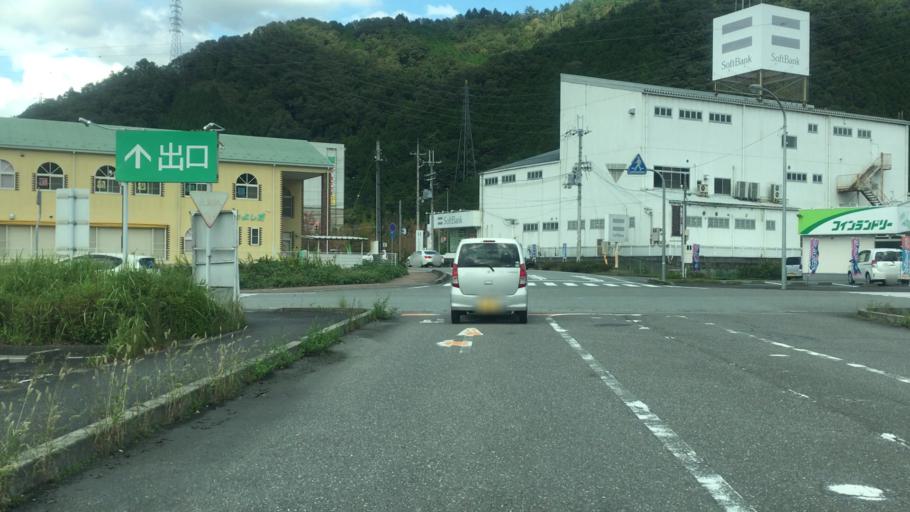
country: JP
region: Hyogo
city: Toyooka
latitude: 35.3304
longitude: 134.8638
